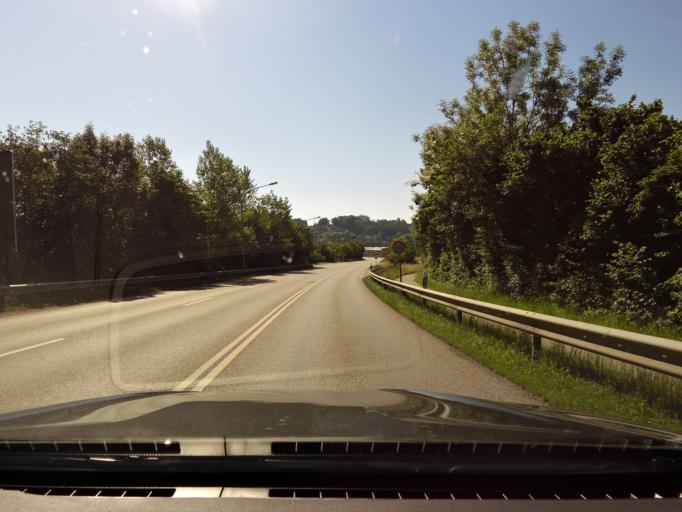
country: DE
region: Bavaria
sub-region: Upper Bavaria
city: Burgkirchen an der Alz
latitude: 48.1757
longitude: 12.7233
